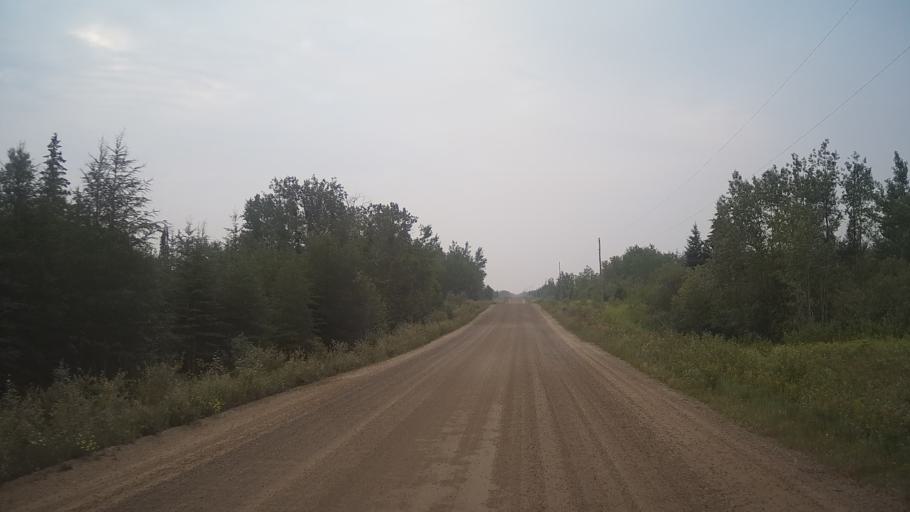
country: CA
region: Ontario
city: Hearst
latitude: 49.6357
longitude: -83.2783
